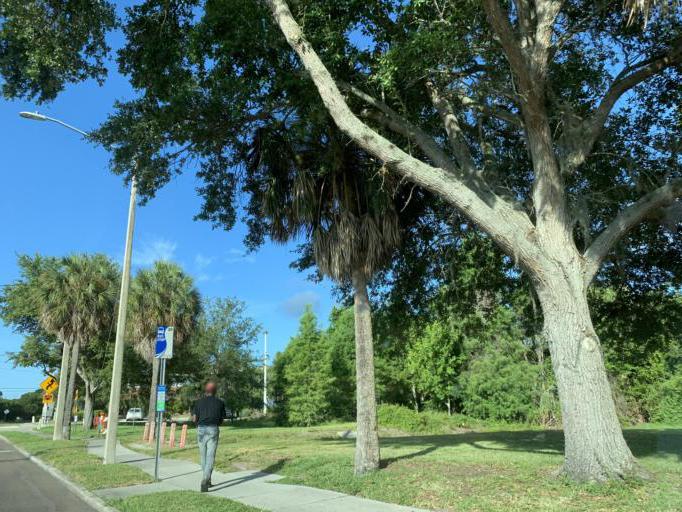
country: US
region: Florida
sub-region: Pinellas County
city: Saint Petersburg
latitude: 27.7272
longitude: -82.6449
